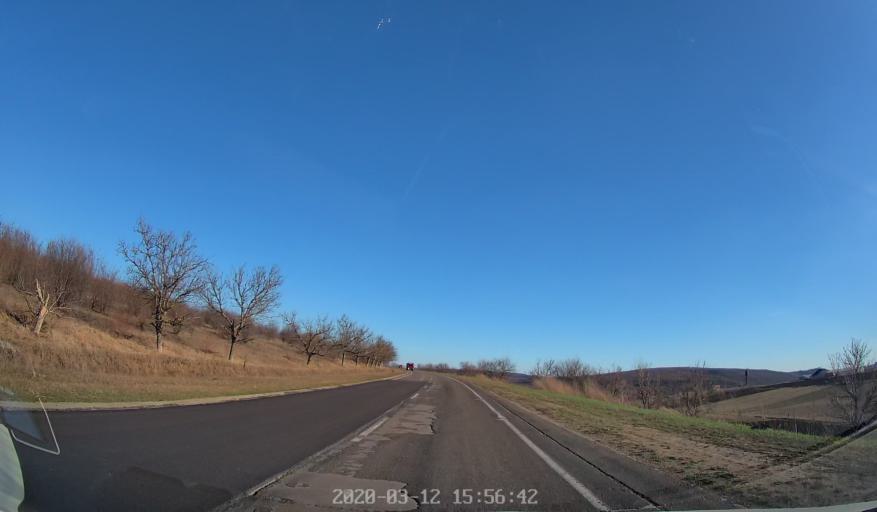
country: MD
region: Chisinau
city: Vadul lui Voda
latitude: 47.0600
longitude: 29.0358
